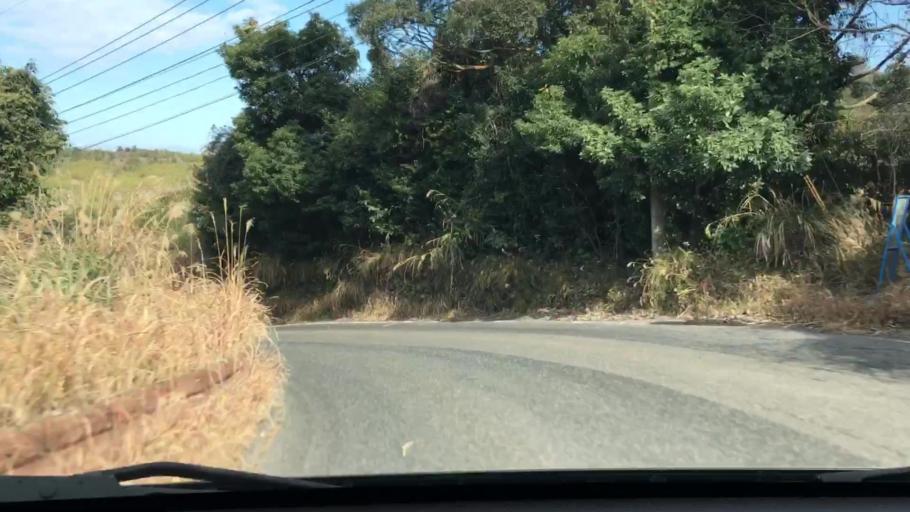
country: JP
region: Kagoshima
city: Tarumizu
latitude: 31.5801
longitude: 130.7056
